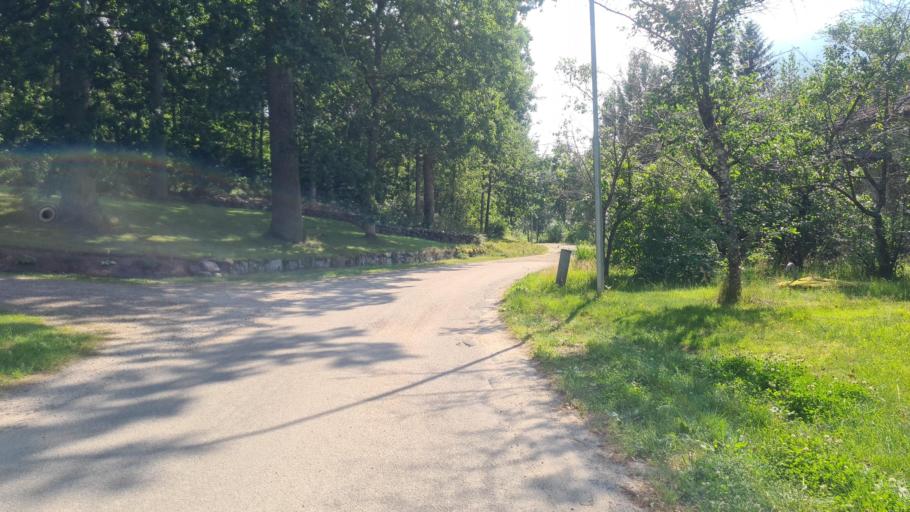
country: SE
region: Kronoberg
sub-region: Ljungby Kommun
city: Ljungby
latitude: 56.7395
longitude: 13.8753
